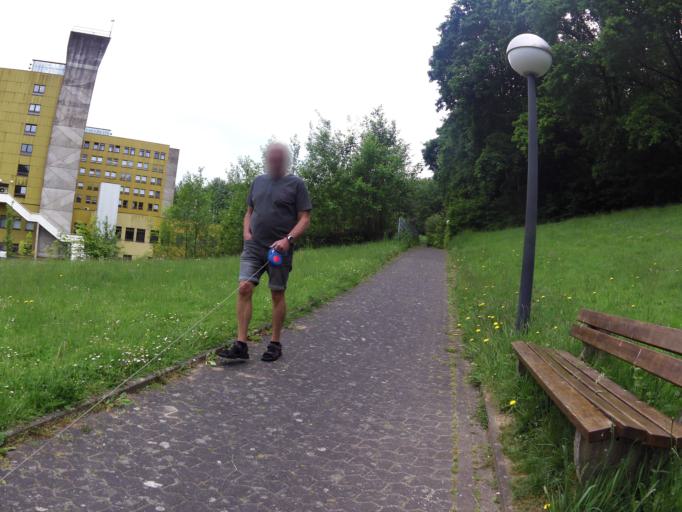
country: DE
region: North Rhine-Westphalia
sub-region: Regierungsbezirk Detmold
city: Hoexter
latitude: 51.7858
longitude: 9.3642
